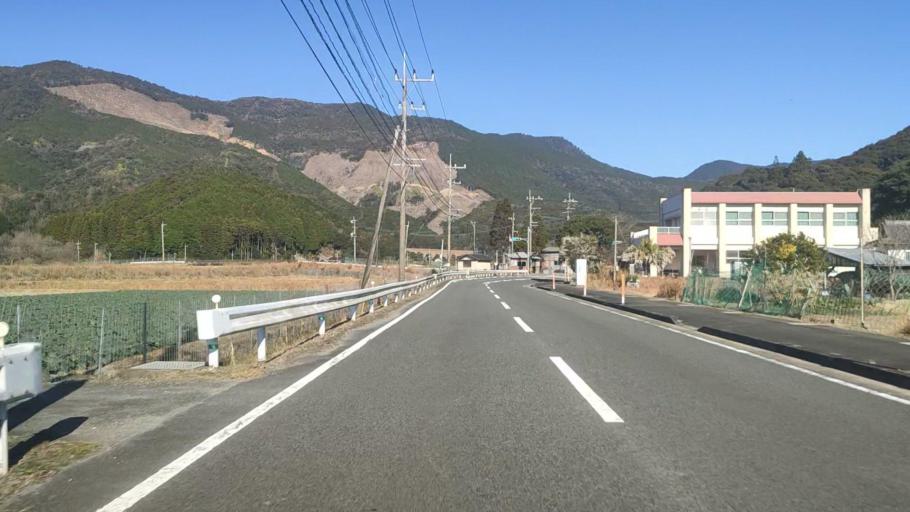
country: JP
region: Miyazaki
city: Nobeoka
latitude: 32.6830
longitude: 131.7872
